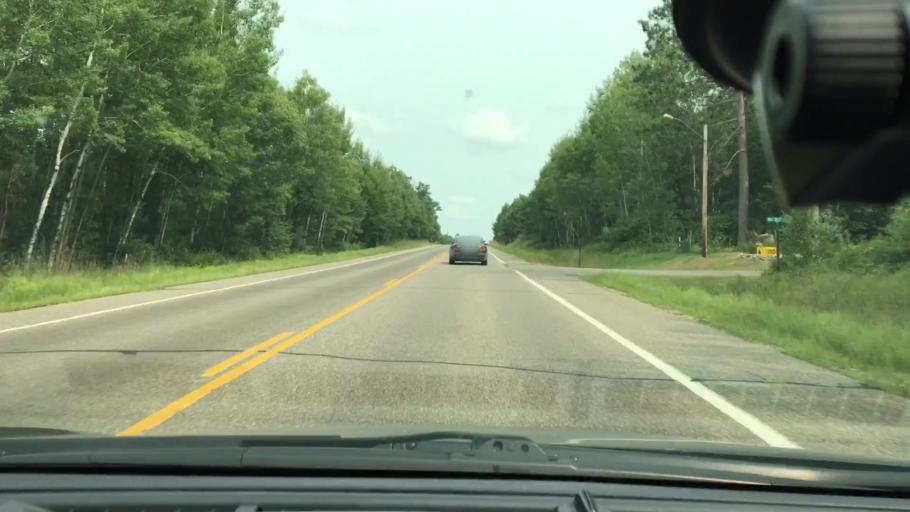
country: US
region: Minnesota
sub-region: Crow Wing County
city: Cross Lake
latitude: 46.7308
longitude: -93.9930
